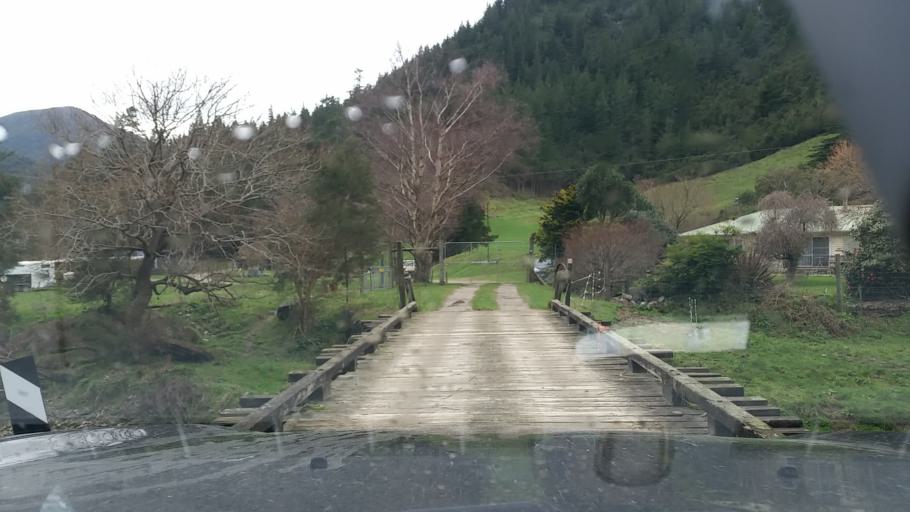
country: NZ
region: Marlborough
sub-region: Marlborough District
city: Blenheim
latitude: -41.3871
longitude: 173.8497
